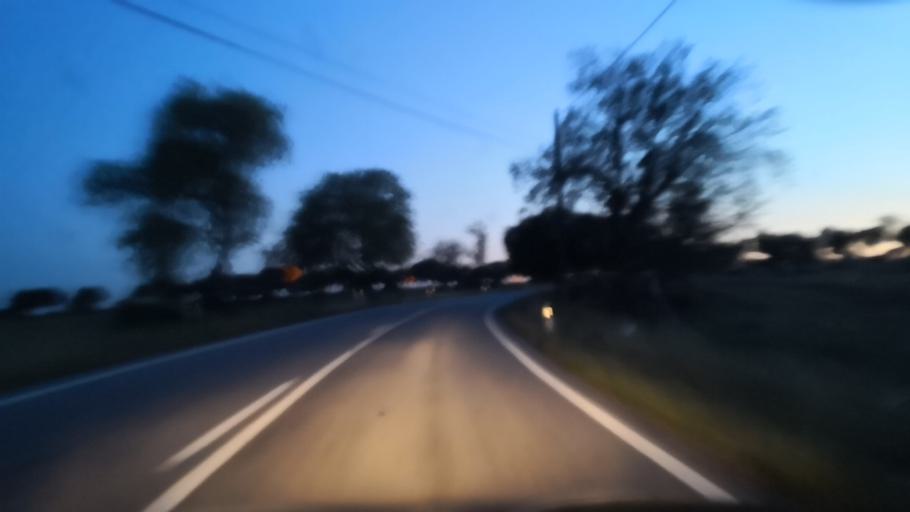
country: ES
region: Extremadura
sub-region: Provincia de Caceres
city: Piedras Albas
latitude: 39.8541
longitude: -7.0469
